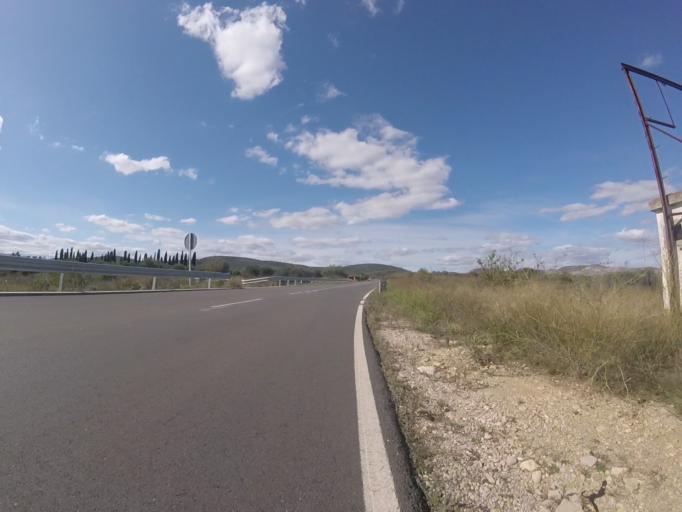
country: ES
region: Valencia
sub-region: Provincia de Castello
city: Chert/Xert
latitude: 40.4271
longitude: 0.1495
